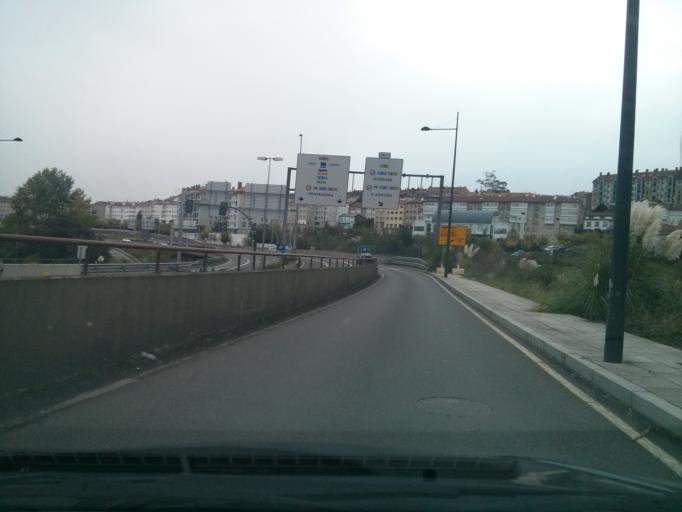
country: ES
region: Galicia
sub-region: Provincia da Coruna
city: Santiago de Compostela
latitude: 42.8698
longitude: -8.5492
